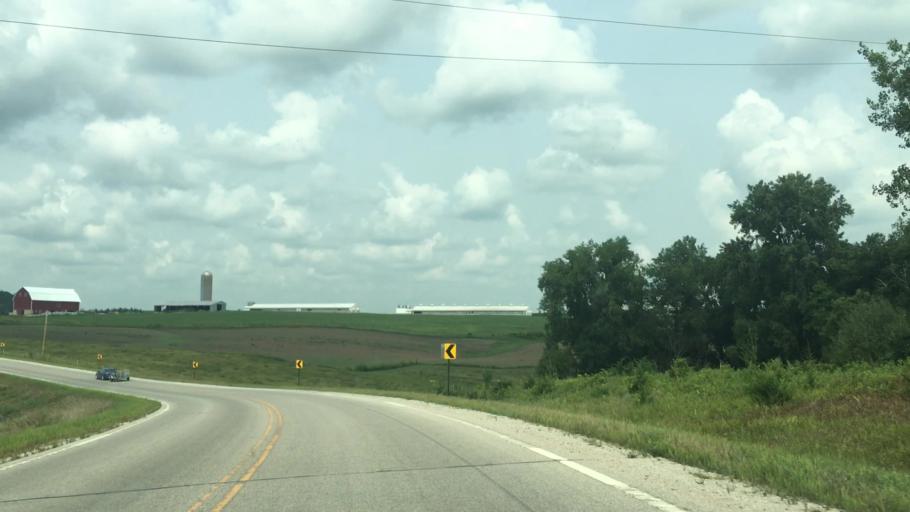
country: US
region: Minnesota
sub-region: Fillmore County
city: Preston
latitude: 43.7319
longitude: -91.9997
